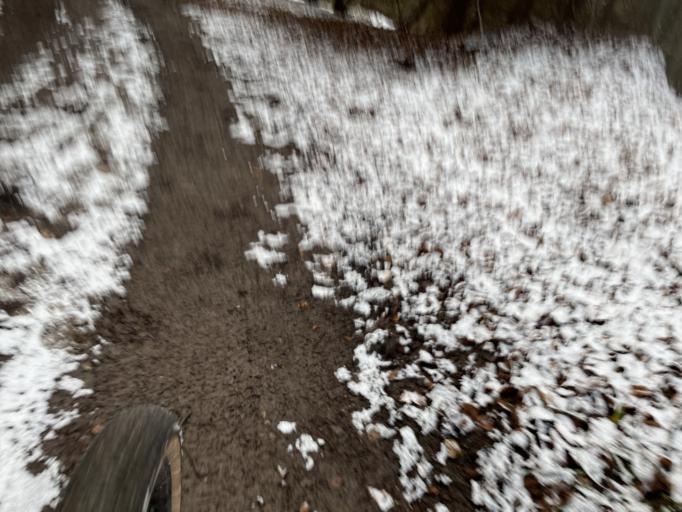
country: CH
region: Lucerne
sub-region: Entlebuch District
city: Oberdiessbach
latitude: 46.8448
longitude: 7.6047
